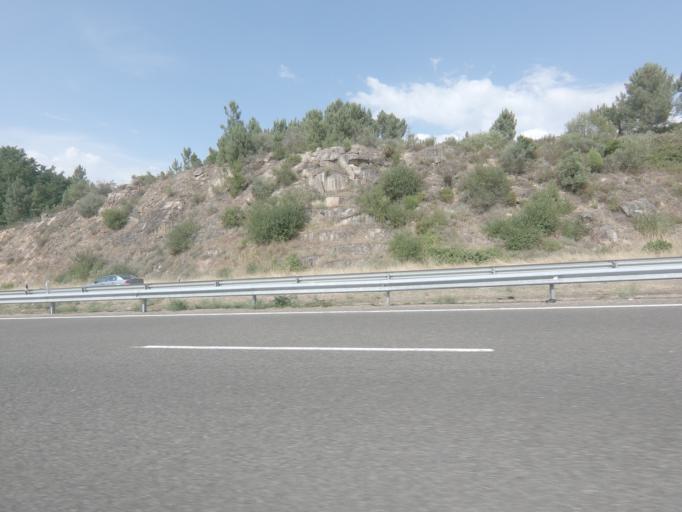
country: ES
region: Galicia
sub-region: Provincia de Ourense
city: Ourense
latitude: 42.2894
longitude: -7.8764
